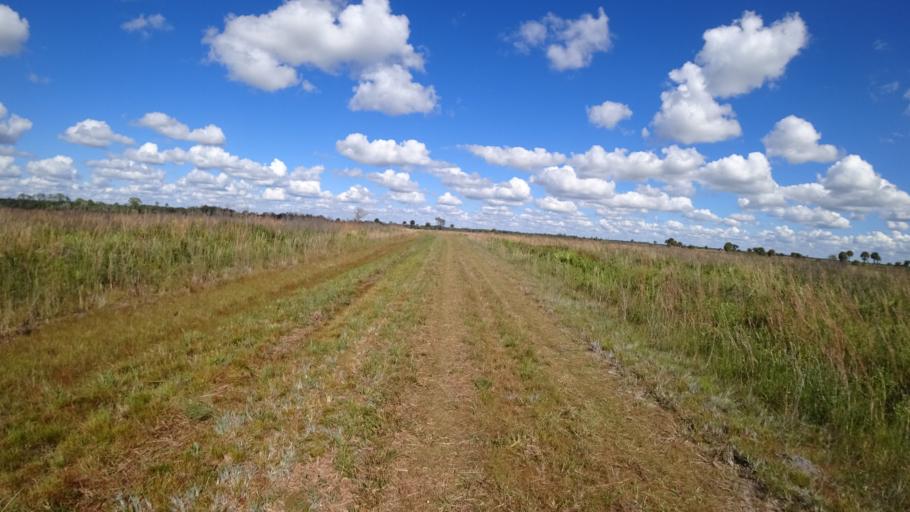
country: US
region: Florida
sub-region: Sarasota County
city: Lake Sarasota
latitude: 27.2646
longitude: -82.2667
